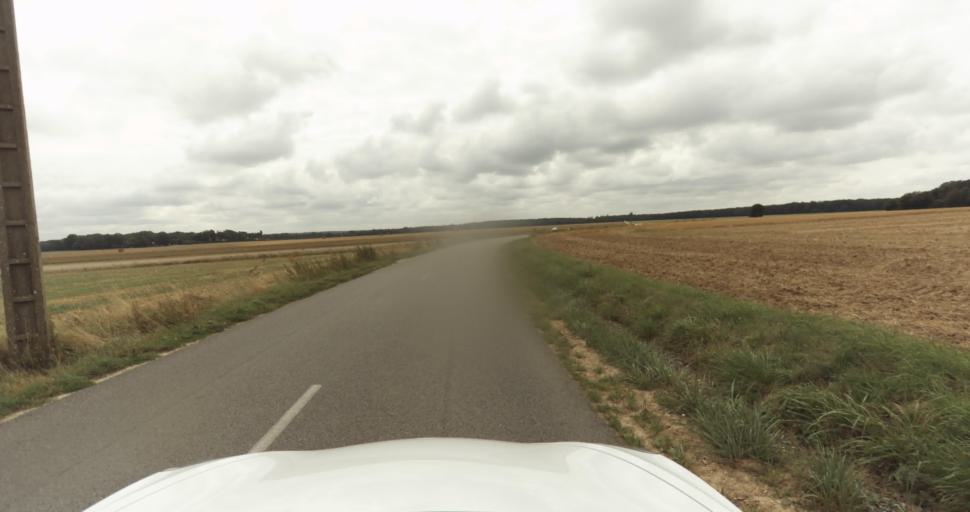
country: FR
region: Haute-Normandie
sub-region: Departement de l'Eure
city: Claville
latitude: 49.0179
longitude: 1.0343
